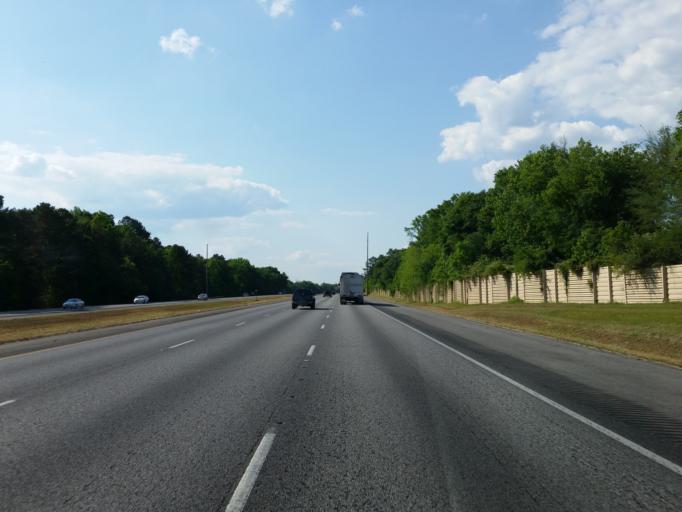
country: US
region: Georgia
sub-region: Bibb County
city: West Point
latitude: 32.7783
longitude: -83.7139
